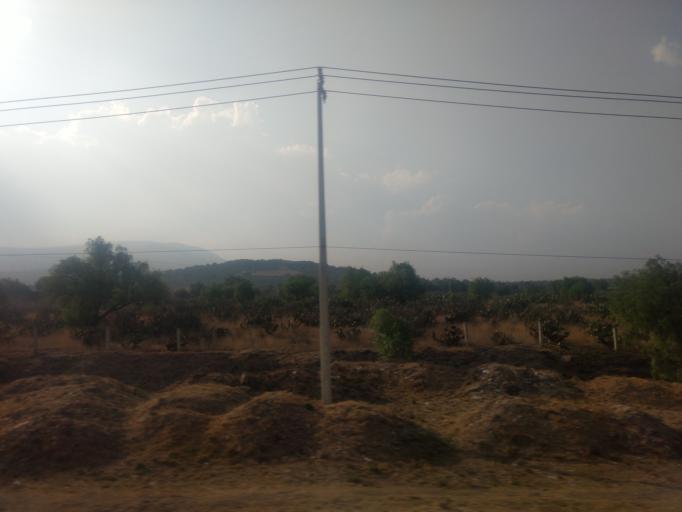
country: MX
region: Morelos
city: Axapusco
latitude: 19.7355
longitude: -98.7725
